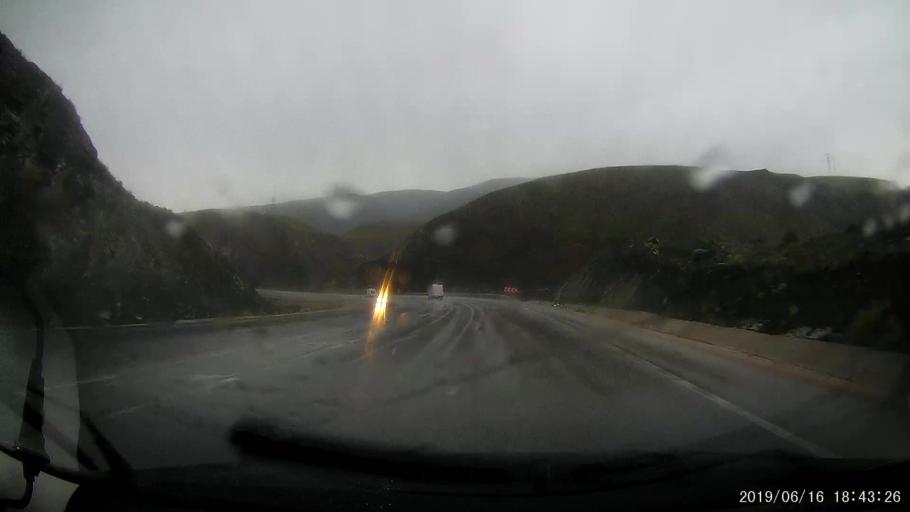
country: TR
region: Erzincan
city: Doganbeyli
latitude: 39.8696
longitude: 39.0916
